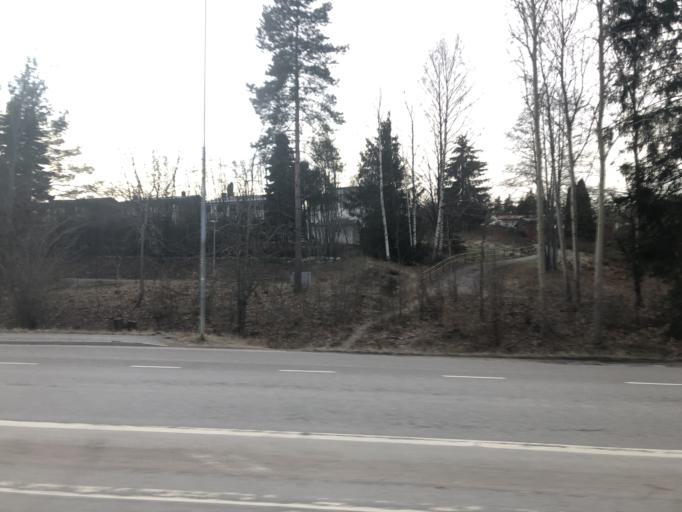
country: SE
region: Stockholm
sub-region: Jarfalla Kommun
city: Jakobsberg
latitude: 59.4104
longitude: 17.7967
